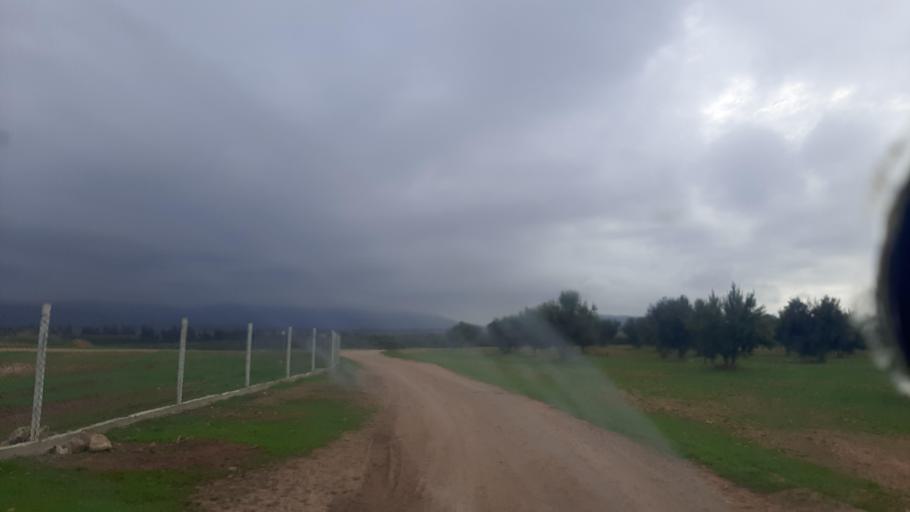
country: TN
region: Tunis
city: La Sebala du Mornag
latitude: 36.5675
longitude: 10.2954
